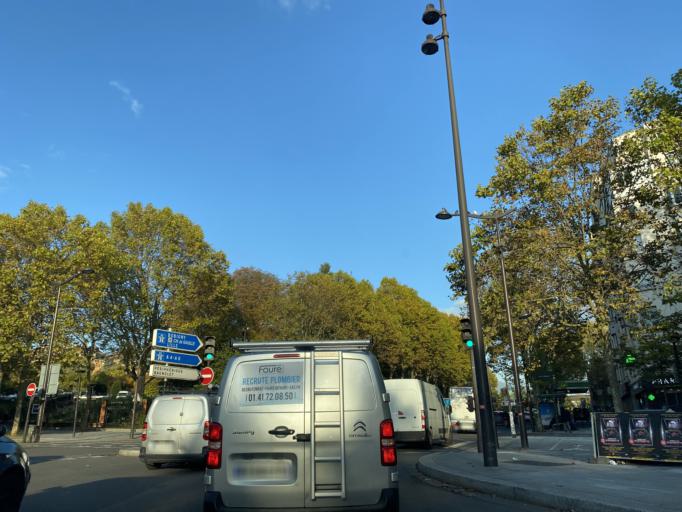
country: FR
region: Ile-de-France
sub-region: Departement de Seine-Saint-Denis
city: Bagnolet
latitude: 48.8644
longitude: 2.4090
